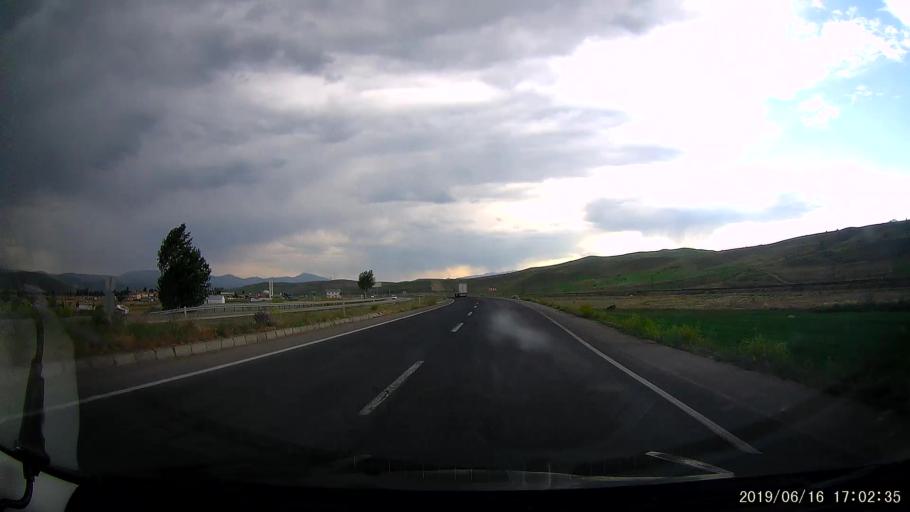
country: TR
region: Erzurum
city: Askale
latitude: 39.9405
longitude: 40.7511
